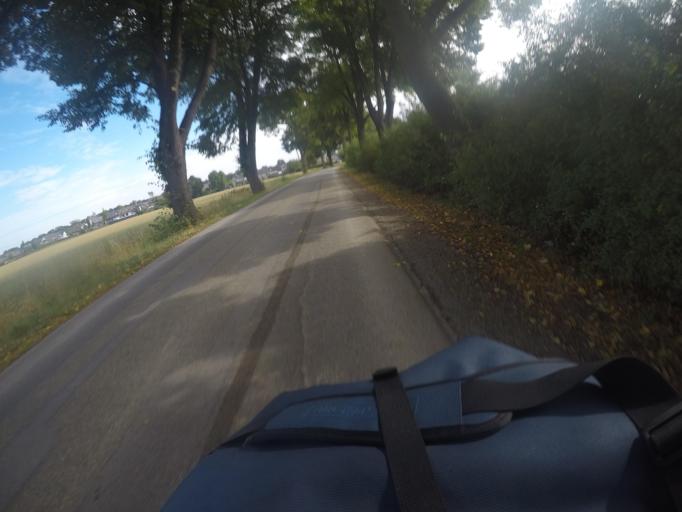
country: DE
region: North Rhine-Westphalia
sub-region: Regierungsbezirk Dusseldorf
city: Emmerich
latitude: 51.8486
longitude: 6.1972
